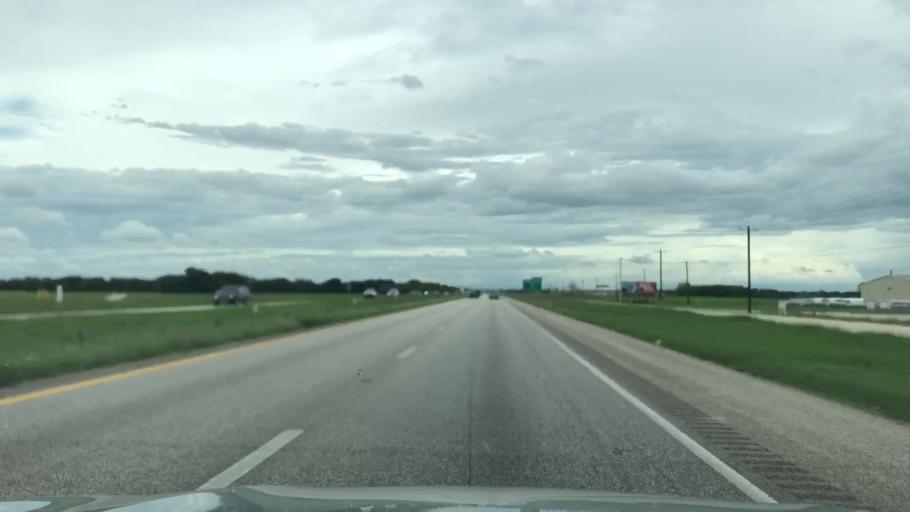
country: US
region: Texas
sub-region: Guadalupe County
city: Marion
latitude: 29.5128
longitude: -98.1564
